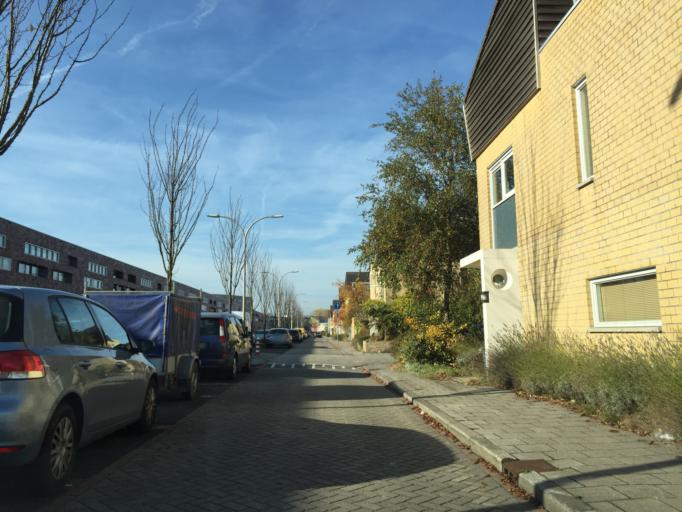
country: NL
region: South Holland
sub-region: Gemeente Pijnacker-Nootdorp
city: Pijnacker
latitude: 52.0042
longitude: 4.3949
